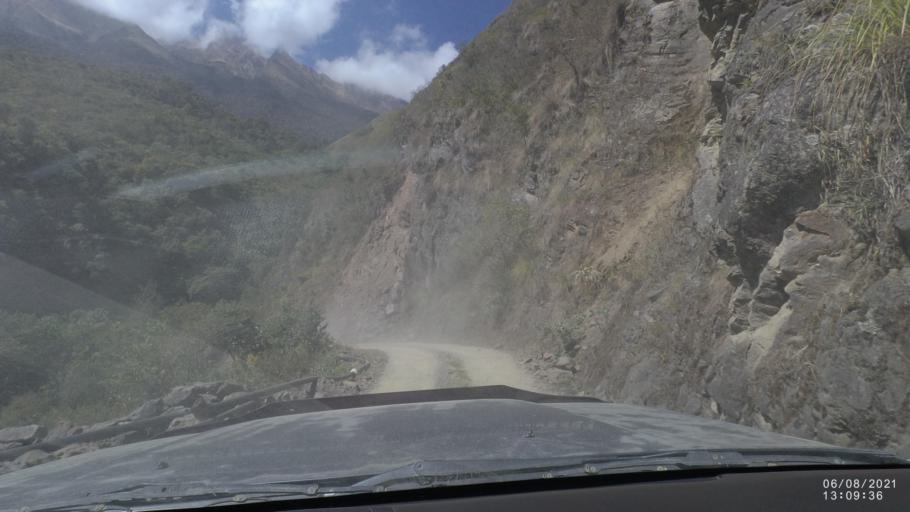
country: BO
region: La Paz
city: Quime
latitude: -16.7265
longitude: -66.7044
